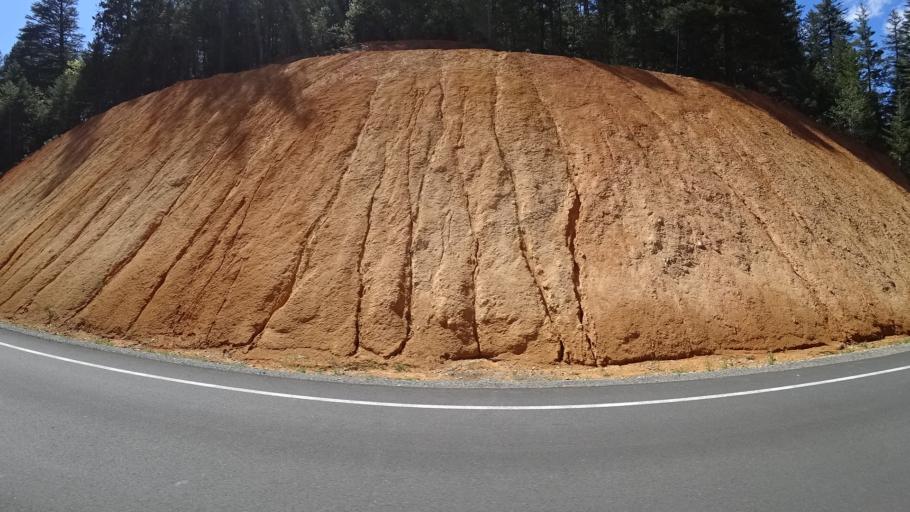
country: US
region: California
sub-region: Trinity County
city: Lewiston
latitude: 40.8891
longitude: -122.7950
